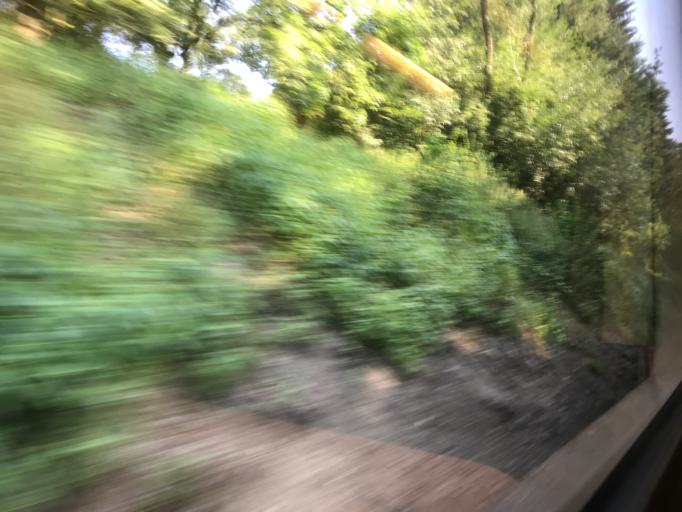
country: CZ
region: Central Bohemia
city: Votice
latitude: 49.6244
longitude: 14.6025
